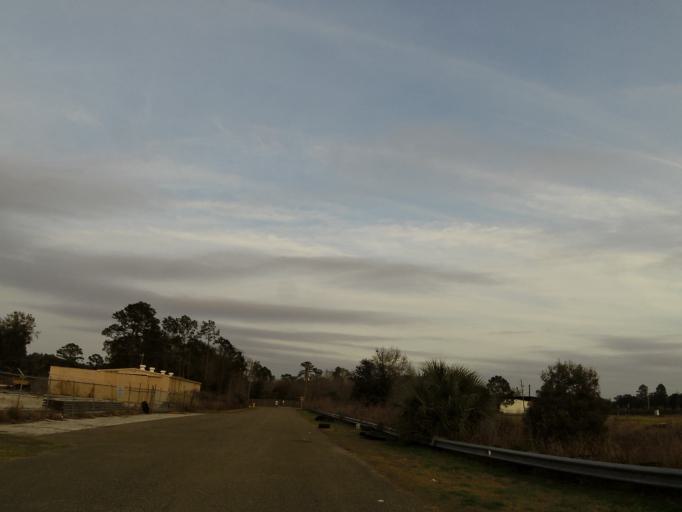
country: US
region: Florida
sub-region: Duval County
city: Jacksonville
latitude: 30.3645
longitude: -81.7130
